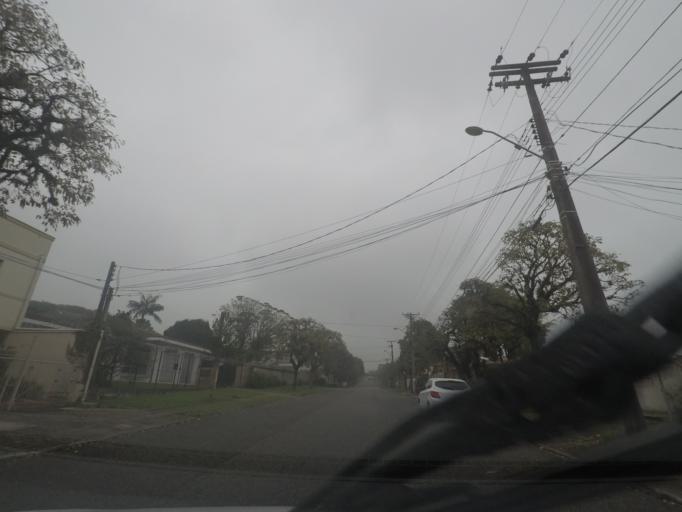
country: BR
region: Parana
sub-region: Curitiba
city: Curitiba
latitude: -25.4564
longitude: -49.2413
